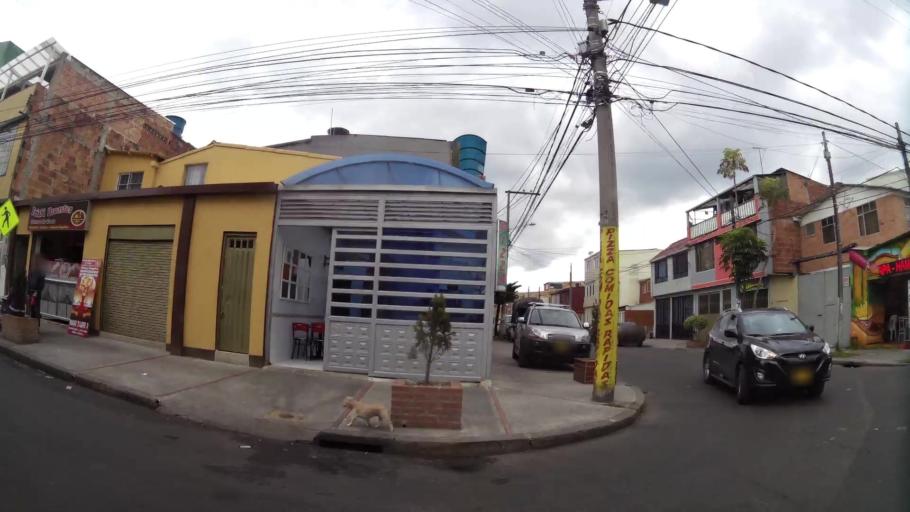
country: CO
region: Bogota D.C.
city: Bogota
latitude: 4.6094
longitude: -74.1350
